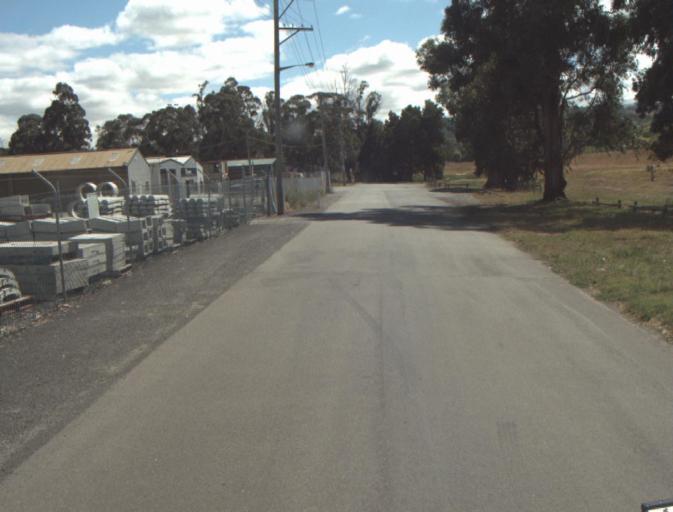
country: AU
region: Tasmania
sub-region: Launceston
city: East Launceston
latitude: -41.4186
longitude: 147.1431
